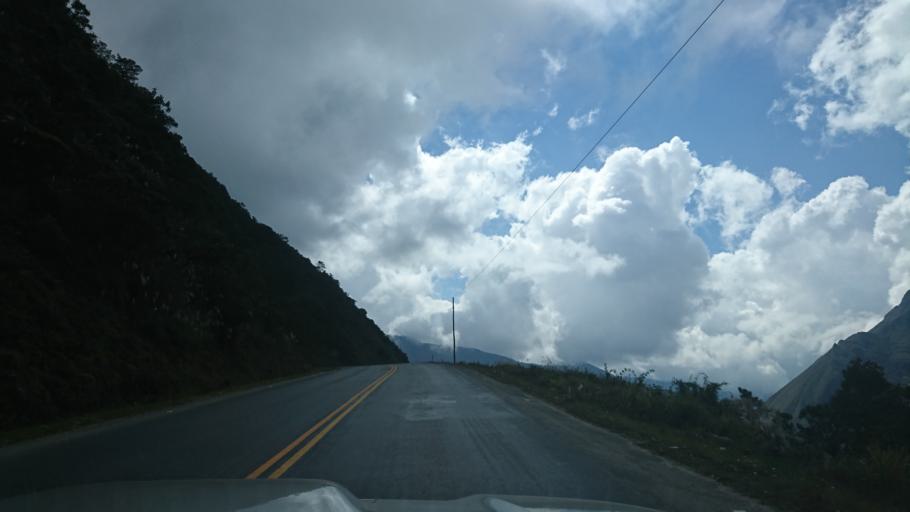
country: BO
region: La Paz
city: Coroico
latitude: -16.3091
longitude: -67.9010
